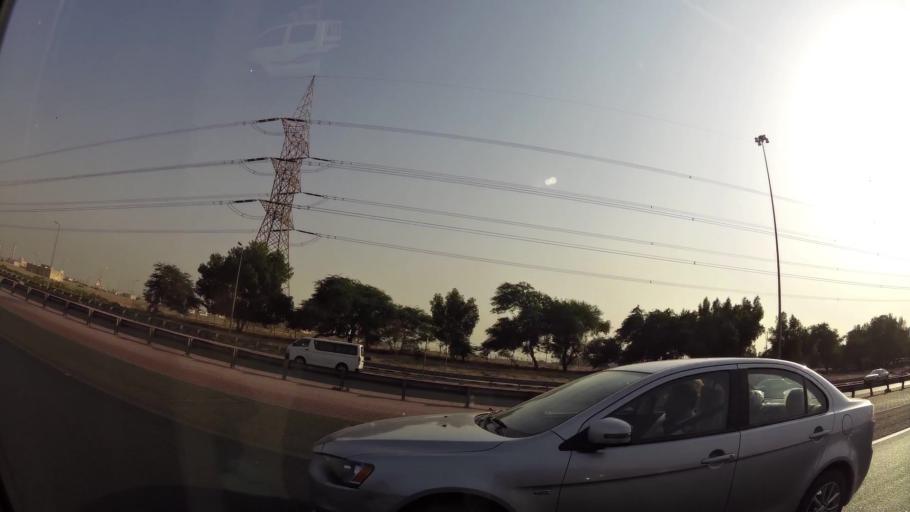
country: KW
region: Al Farwaniyah
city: Janub as Surrah
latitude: 29.3042
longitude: 47.9836
